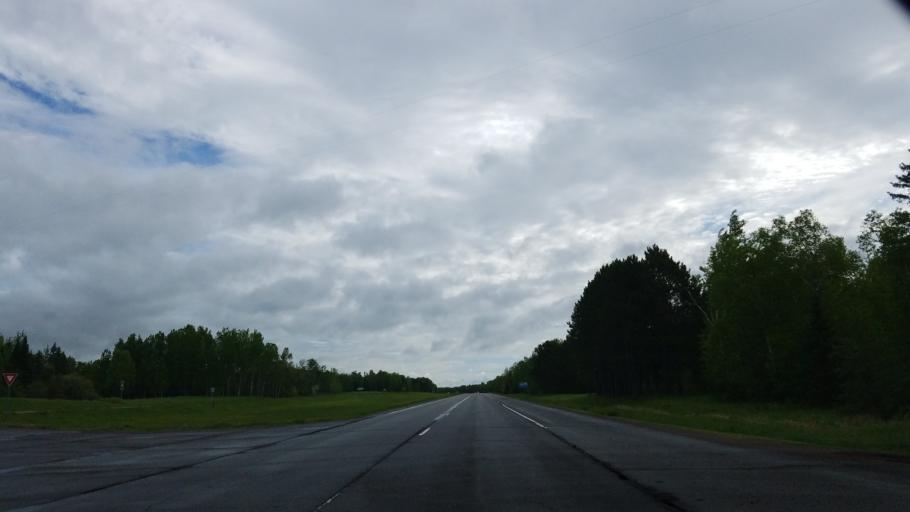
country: US
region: Minnesota
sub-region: Saint Louis County
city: Arnold
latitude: 46.8890
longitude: -91.9216
